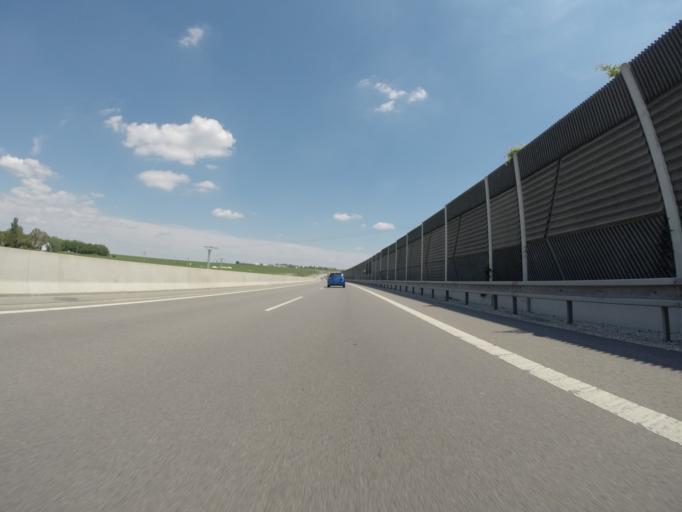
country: SK
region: Nitriansky
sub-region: Okres Nitra
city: Nitra
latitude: 48.2970
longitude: 18.0275
